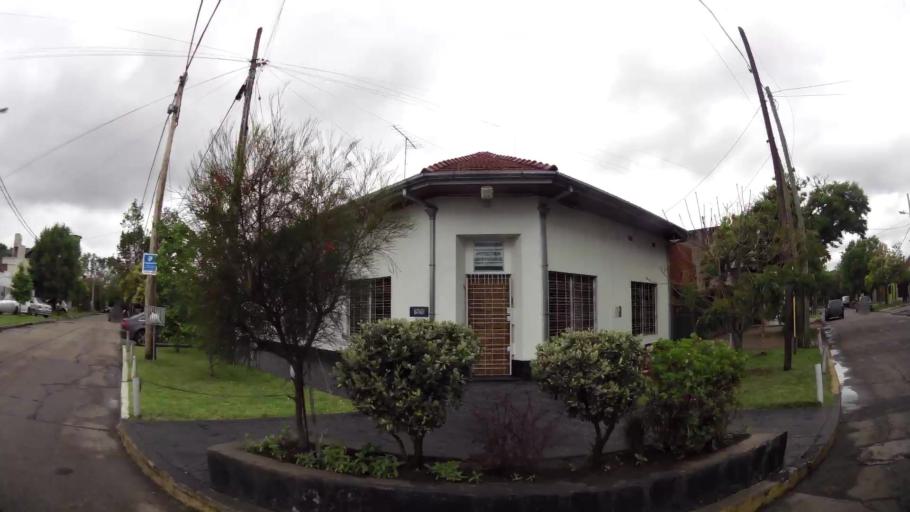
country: AR
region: Buenos Aires
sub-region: Partido de Lomas de Zamora
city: Lomas de Zamora
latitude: -34.7563
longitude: -58.3878
